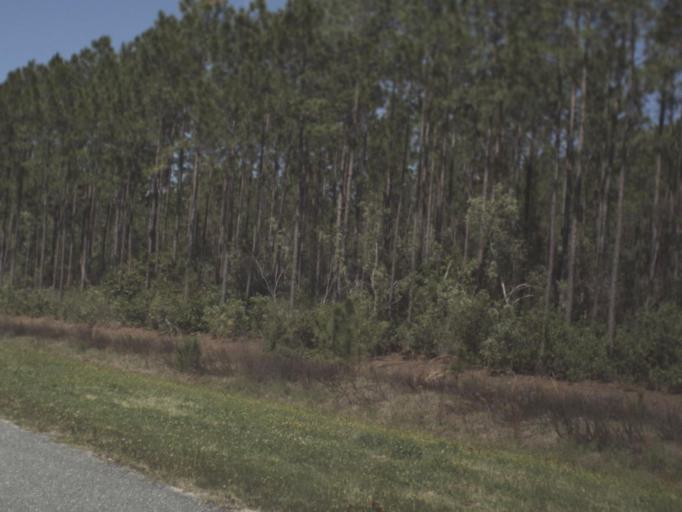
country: US
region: Florida
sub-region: Gulf County
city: Port Saint Joe
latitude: 29.8873
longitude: -85.3471
